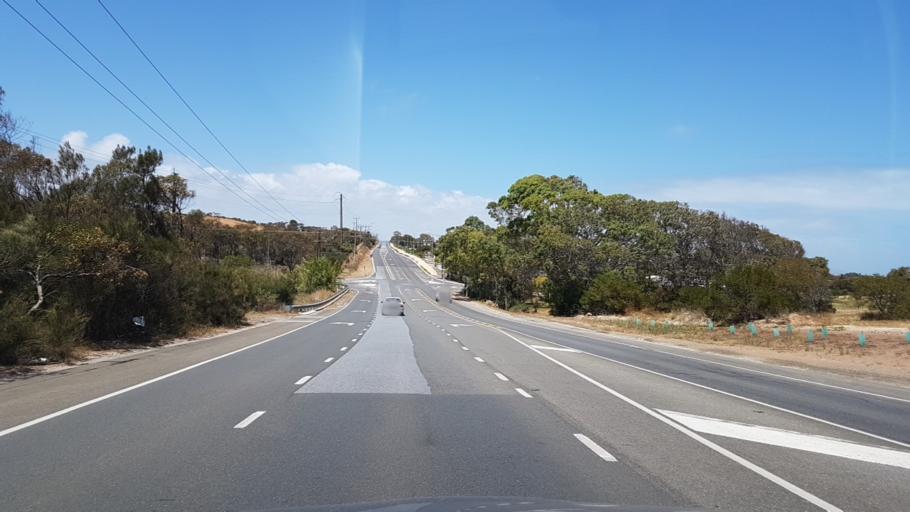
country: AU
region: South Australia
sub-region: Onkaparinga
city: Moana
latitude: -35.2214
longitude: 138.4799
